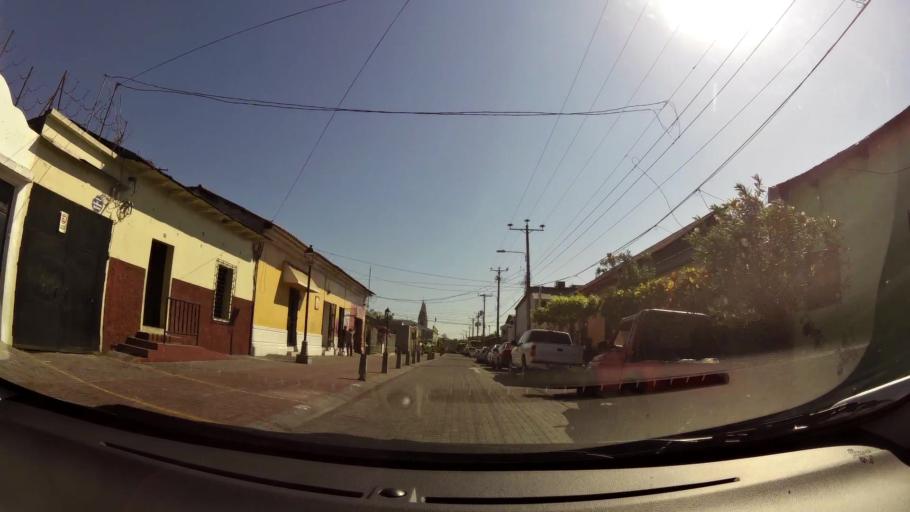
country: SV
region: La Libertad
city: Santa Tecla
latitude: 13.6755
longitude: -89.2908
